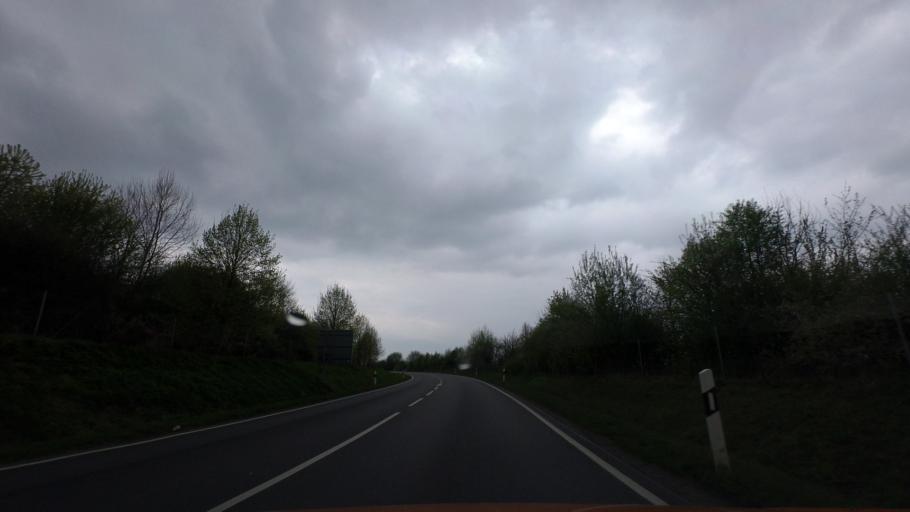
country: DE
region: Lower Saxony
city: Bersenbruck
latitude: 52.5353
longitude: 7.9416
